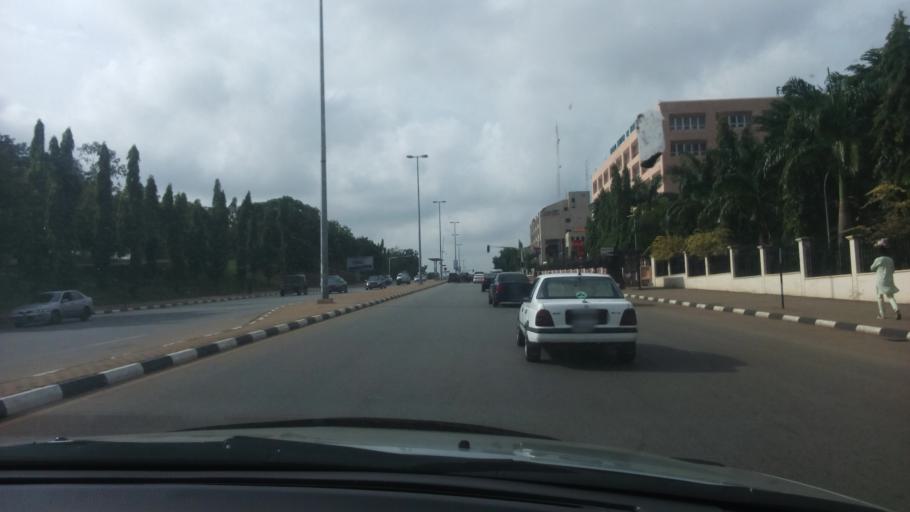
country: NG
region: Abuja Federal Capital Territory
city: Abuja
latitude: 9.0676
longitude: 7.4964
